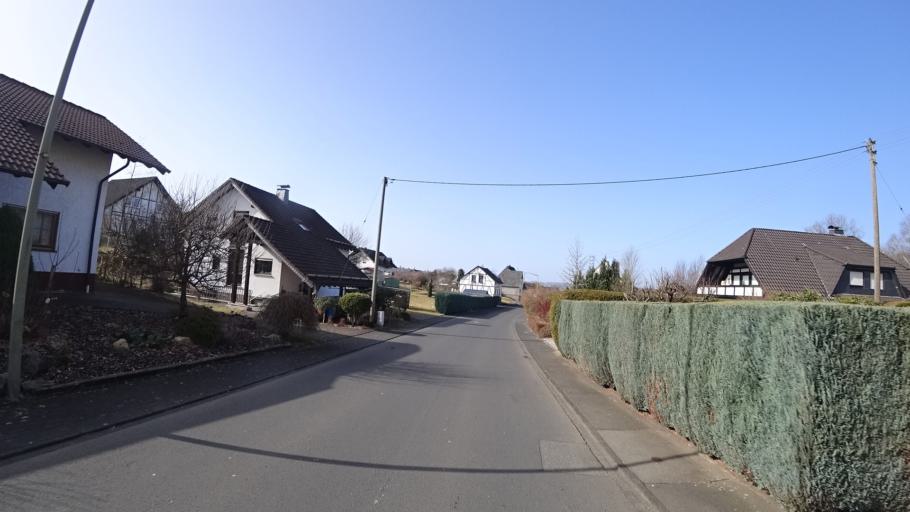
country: DE
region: Rheinland-Pfalz
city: Wissen
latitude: 50.7733
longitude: 7.7655
